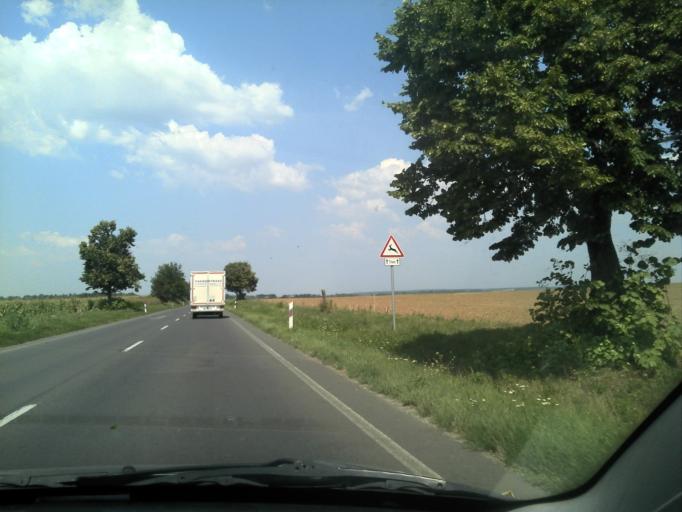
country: HU
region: Tolna
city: Dombovar
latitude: 46.4450
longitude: 18.1594
